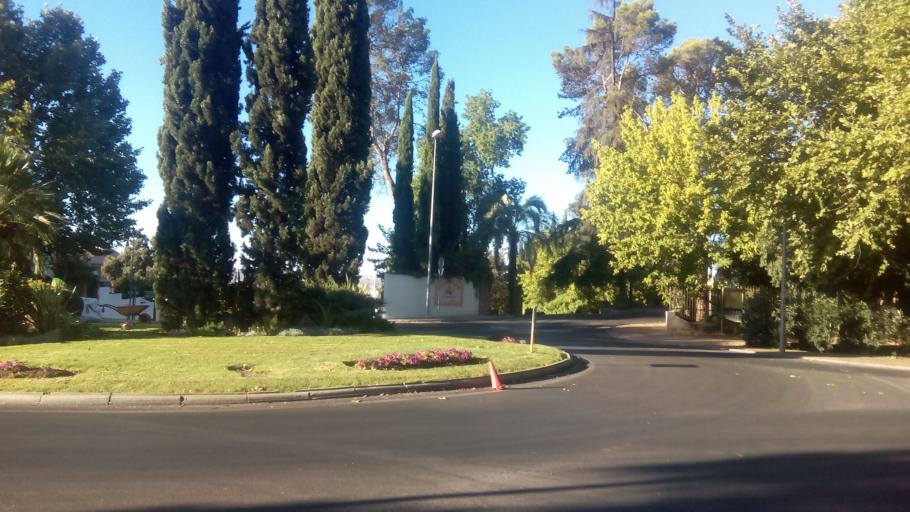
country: ES
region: Andalusia
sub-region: Province of Cordoba
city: Cordoba
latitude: 37.9071
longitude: -4.7987
